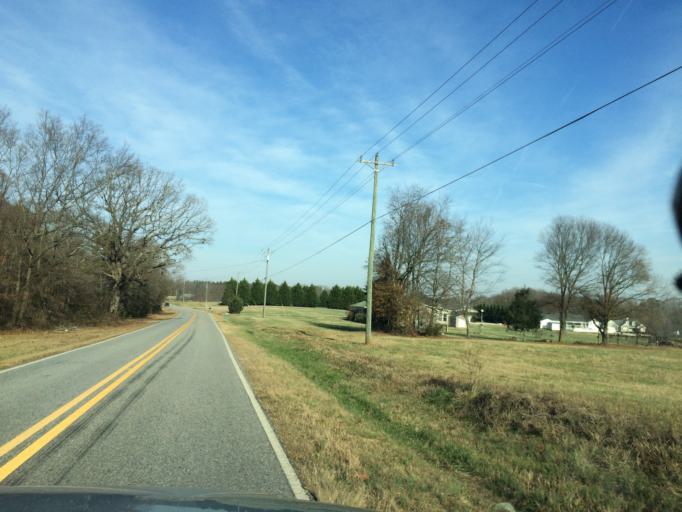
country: US
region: Georgia
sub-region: Hart County
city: Hartwell
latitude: 34.3956
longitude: -83.0048
